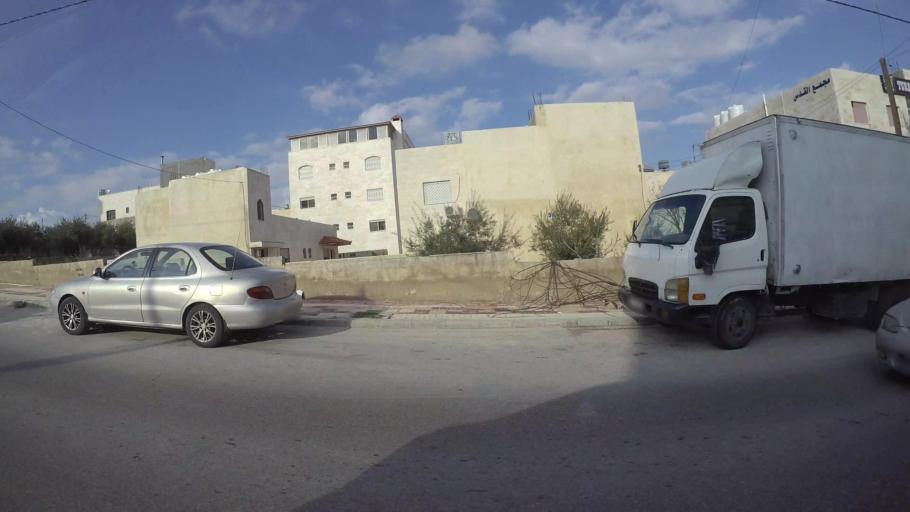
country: JO
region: Amman
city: Al Jubayhah
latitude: 31.9862
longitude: 35.8573
